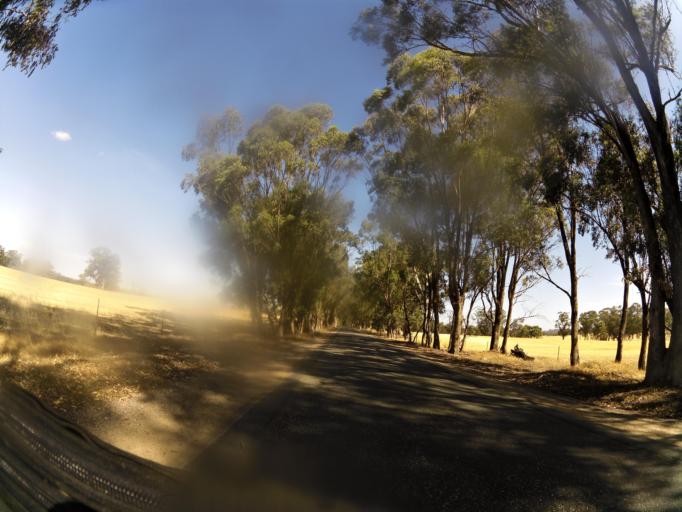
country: AU
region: Victoria
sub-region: Campaspe
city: Kyabram
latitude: -36.8896
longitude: 145.1034
